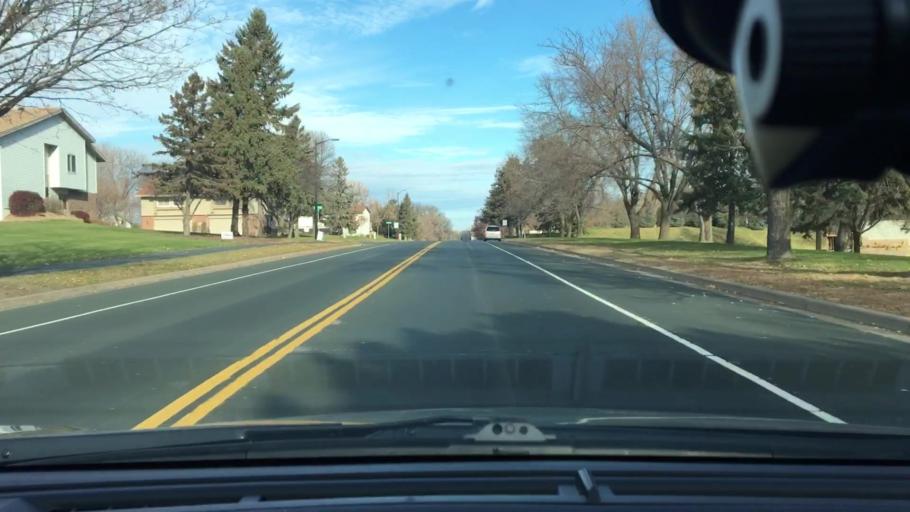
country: US
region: Minnesota
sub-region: Hennepin County
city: Maple Grove
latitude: 45.0966
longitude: -93.4548
